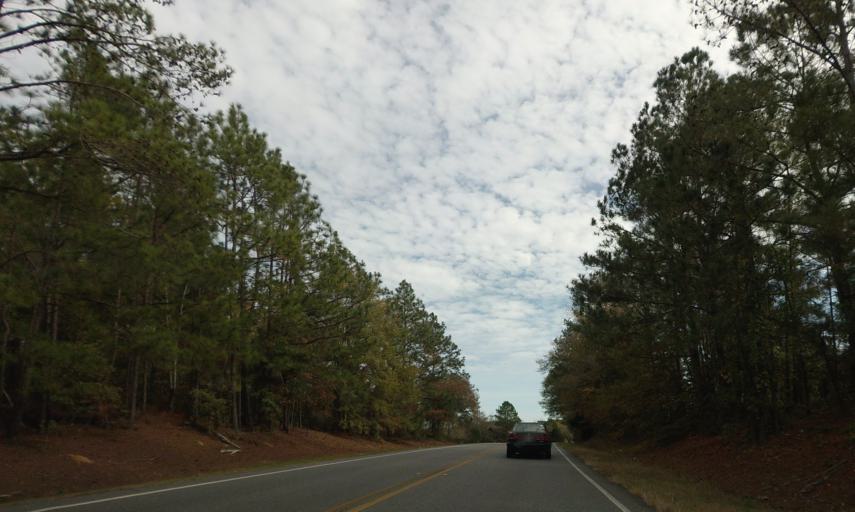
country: US
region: Georgia
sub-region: Dodge County
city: Chester
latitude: 32.4104
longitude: -83.2460
